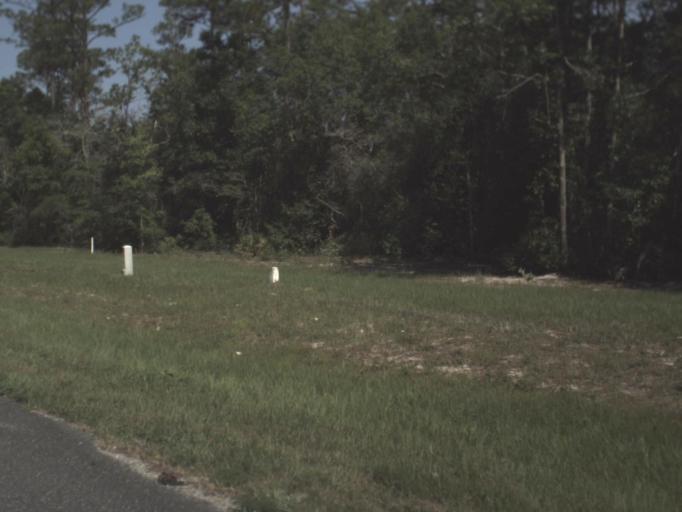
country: US
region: Florida
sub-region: Clay County
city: Green Cove Springs
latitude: 29.9835
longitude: -81.7409
